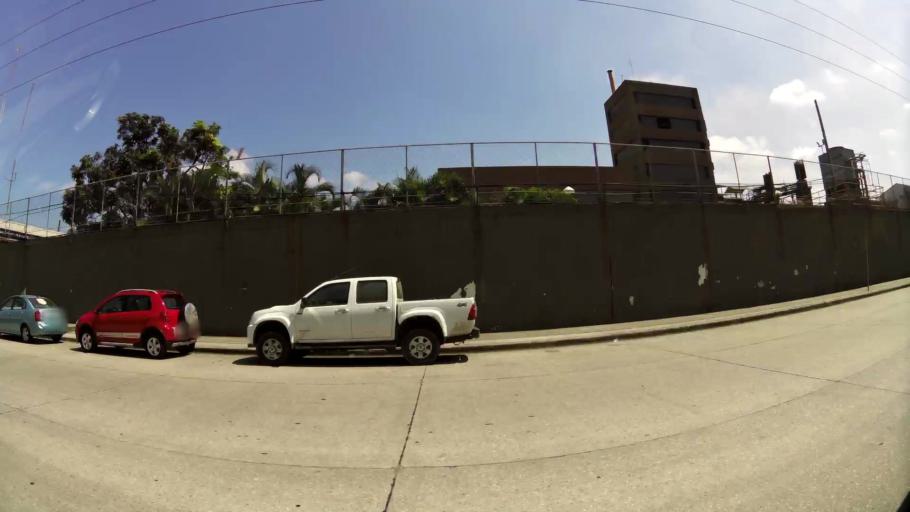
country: EC
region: Guayas
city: Guayaquil
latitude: -2.1411
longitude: -79.9104
